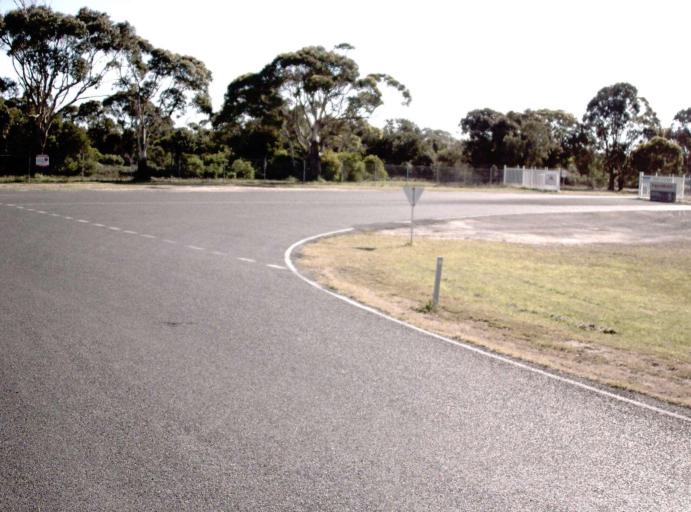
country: AU
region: Victoria
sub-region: Latrobe
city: Morwell
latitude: -38.7102
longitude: 146.3968
